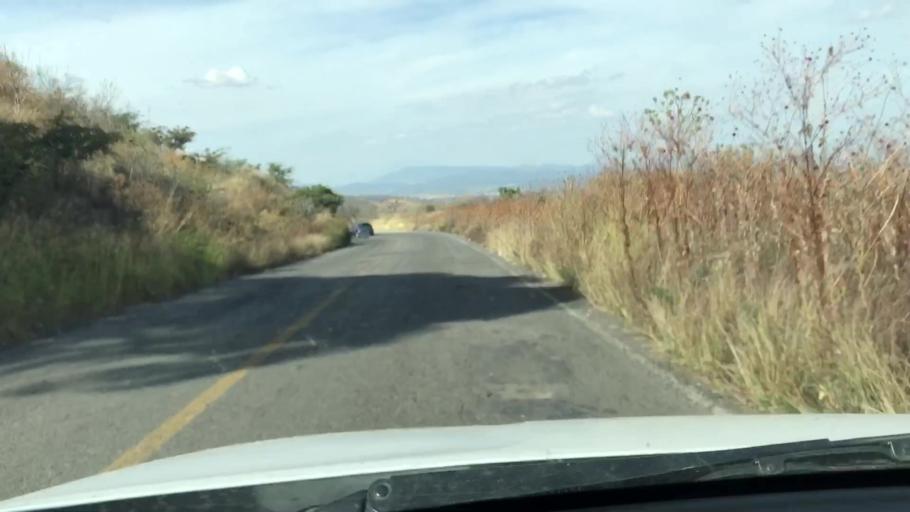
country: MX
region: Jalisco
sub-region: Zacoalco de Torres
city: Barranca de Otates (Barranca de Otatan)
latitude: 20.2489
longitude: -103.6677
